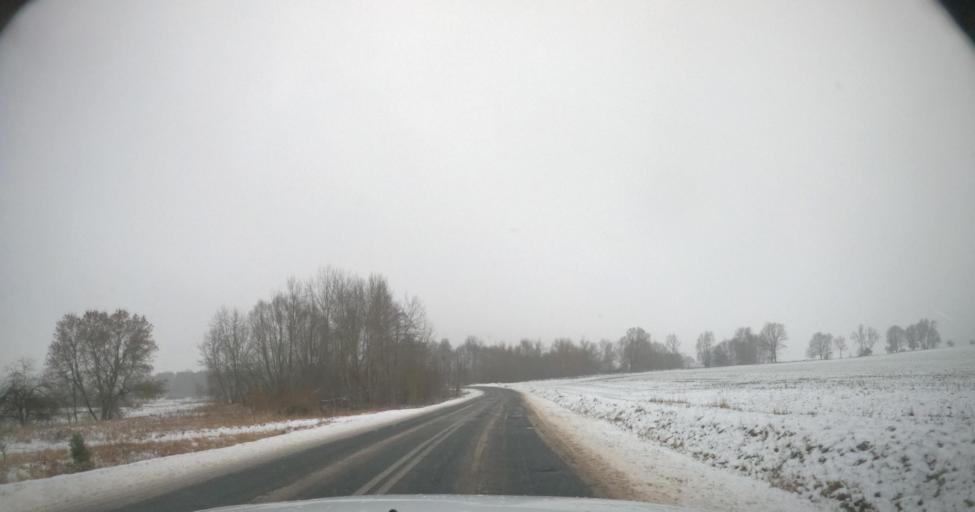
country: PL
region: West Pomeranian Voivodeship
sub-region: Powiat gryficki
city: Brojce
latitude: 53.9017
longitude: 15.2979
